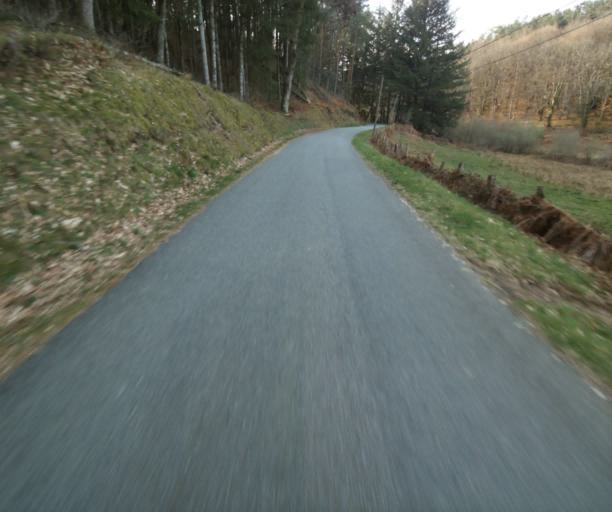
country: FR
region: Limousin
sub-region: Departement de la Correze
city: Correze
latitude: 45.3824
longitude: 1.8571
